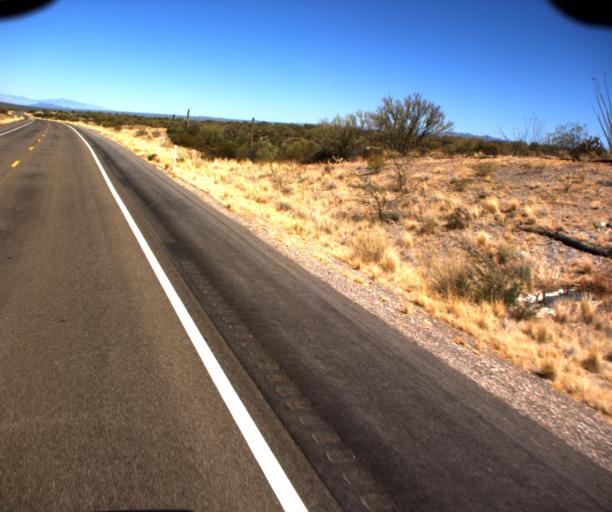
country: US
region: Arizona
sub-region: Pima County
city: Three Points
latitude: 32.0376
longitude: -111.5115
